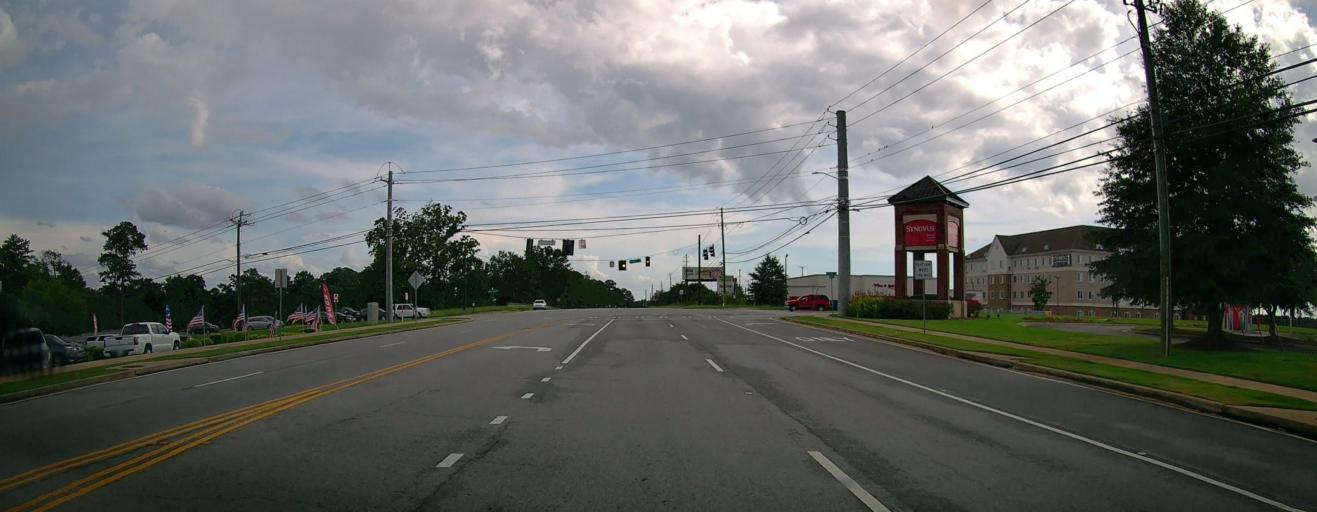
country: US
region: Alabama
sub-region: Russell County
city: Phenix City
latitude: 32.5403
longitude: -84.9667
